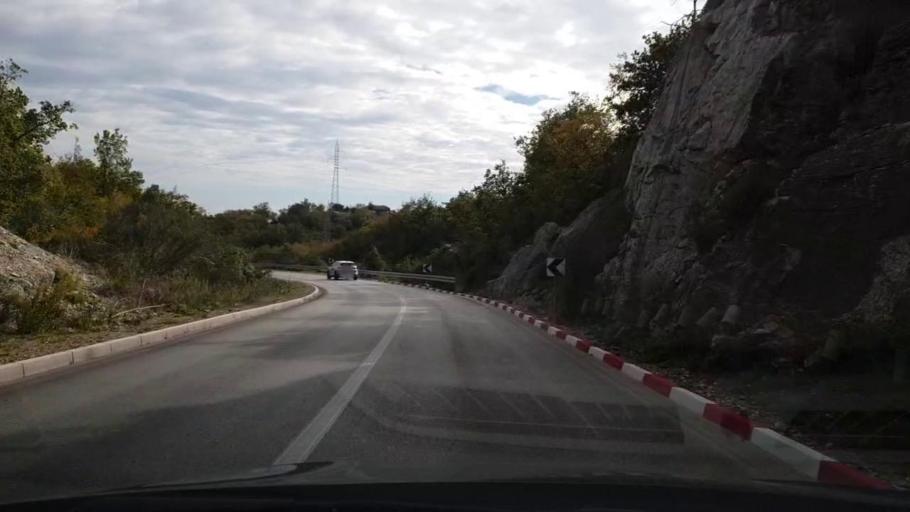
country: ME
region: Herceg Novi
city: Herceg-Novi
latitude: 42.4746
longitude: 18.5288
